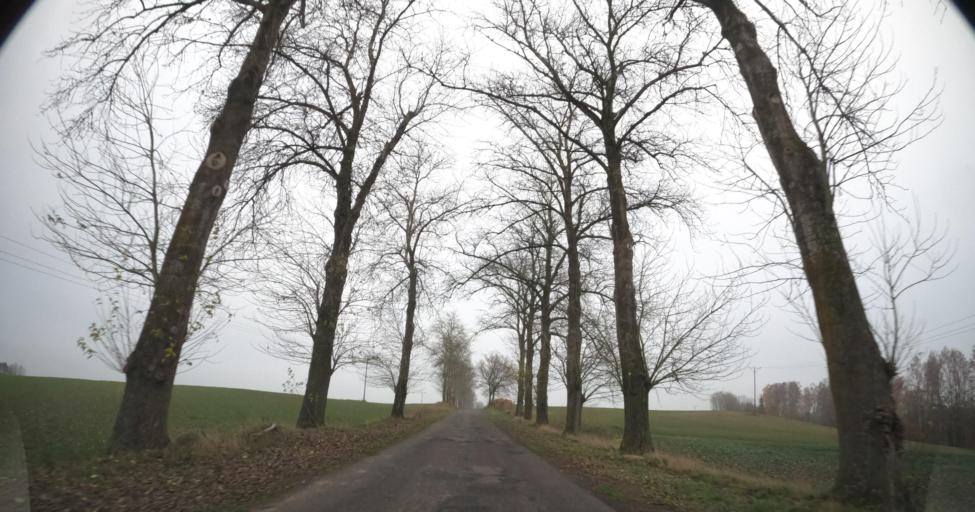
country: PL
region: West Pomeranian Voivodeship
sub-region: Powiat lobeski
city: Wegorzyno
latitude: 53.5434
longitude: 15.6254
